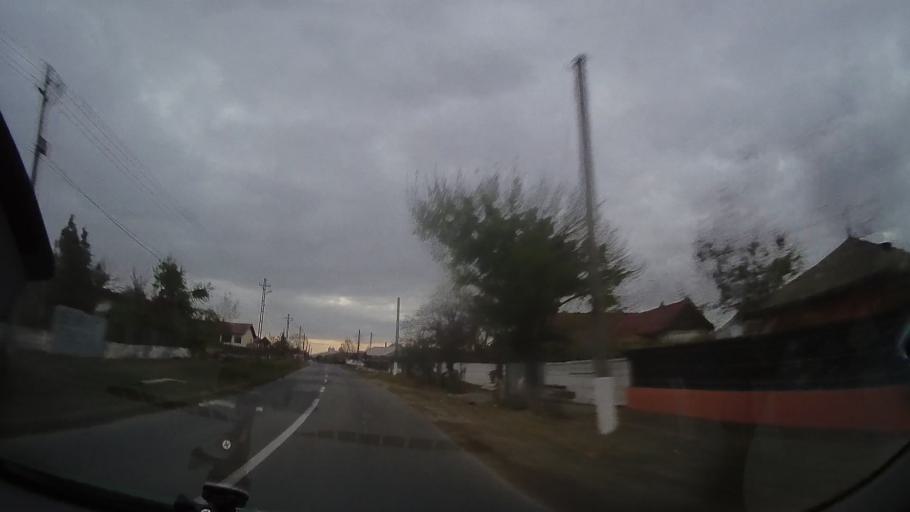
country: RO
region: Tulcea
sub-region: Comuna Mihai Bravu
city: Turda
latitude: 44.9721
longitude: 28.6269
